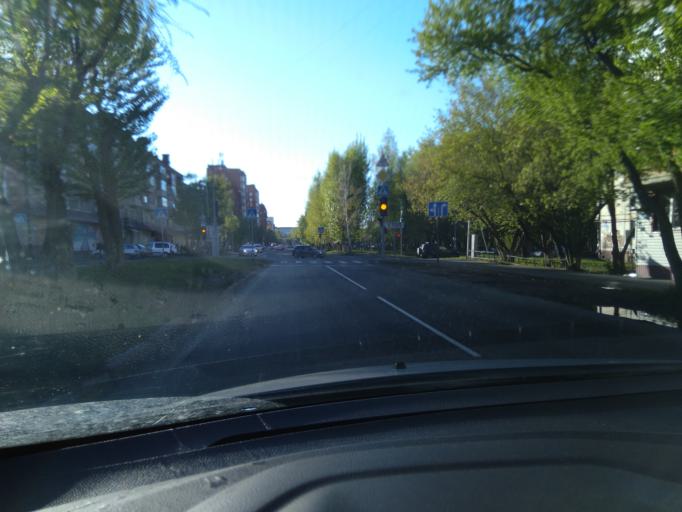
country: RU
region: Tjumen
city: Tyumen
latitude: 57.1324
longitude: 65.5858
